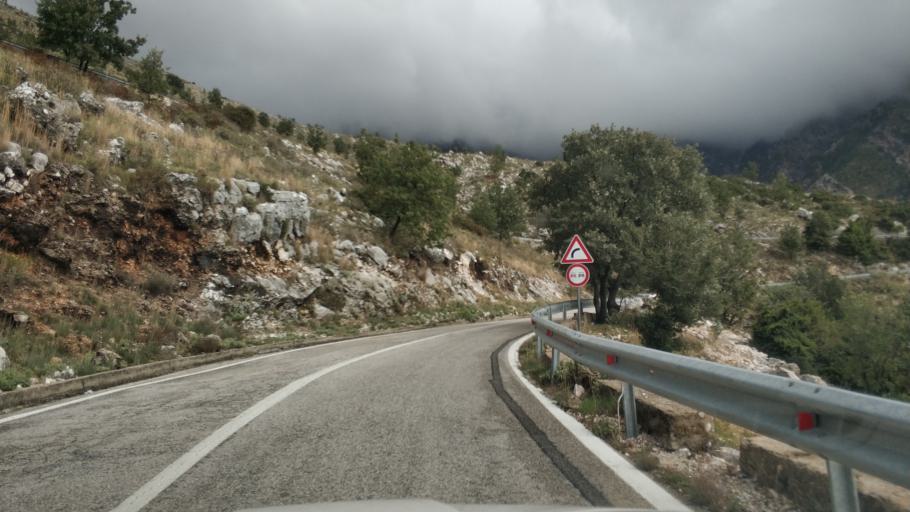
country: AL
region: Vlore
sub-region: Rrethi i Vlores
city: Vranisht
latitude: 40.1855
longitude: 19.6089
